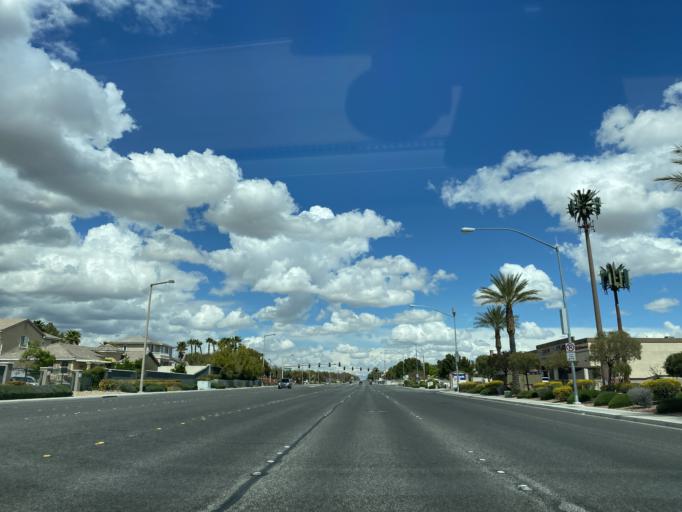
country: US
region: Nevada
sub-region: Clark County
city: Summerlin South
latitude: 36.1280
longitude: -115.3151
